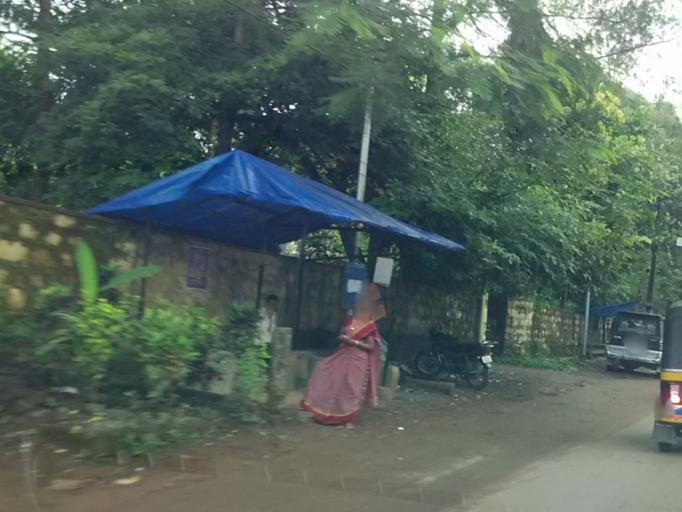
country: IN
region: Kerala
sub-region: Kozhikode
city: Kunnamangalam
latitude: 11.3055
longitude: 75.8926
